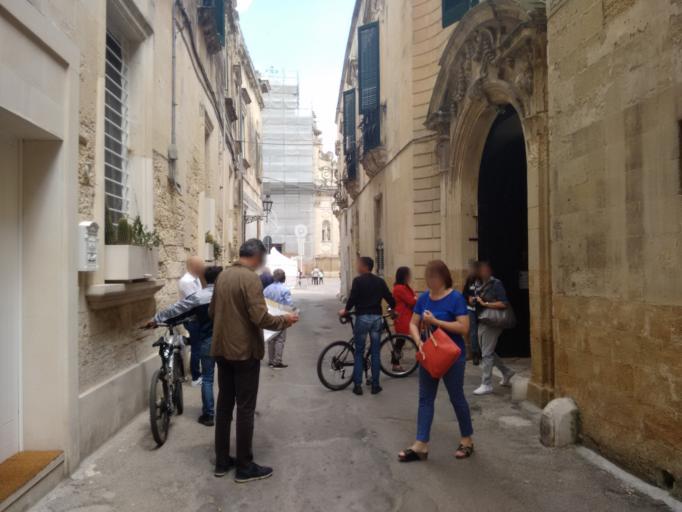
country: IT
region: Apulia
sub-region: Provincia di Lecce
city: Lecce
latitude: 40.3559
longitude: 18.1701
